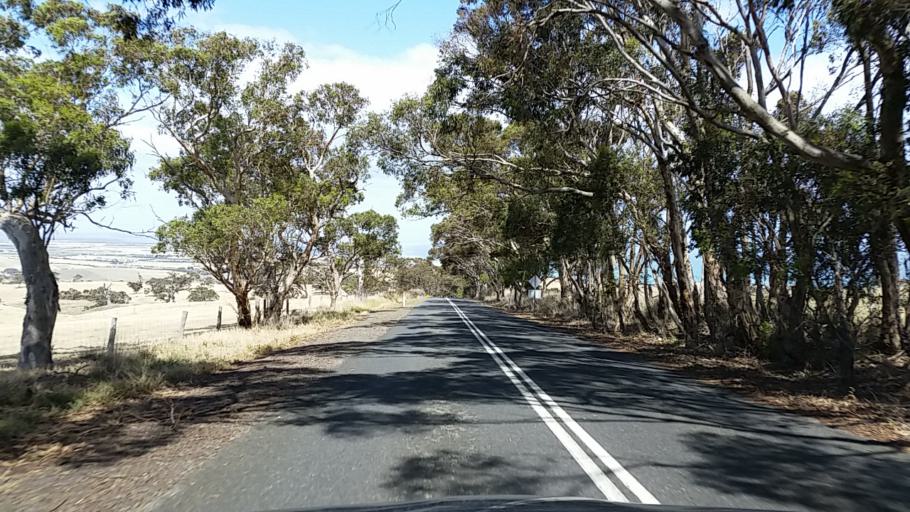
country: AU
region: South Australia
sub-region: Alexandrina
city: Port Elliot
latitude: -35.4966
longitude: 138.6586
